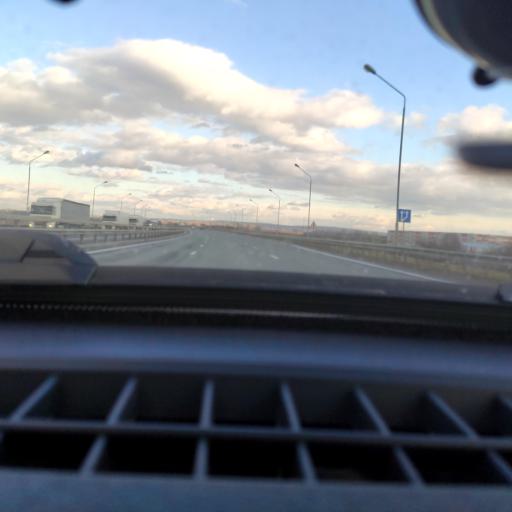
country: RU
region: Bashkortostan
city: Ufa
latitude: 54.6429
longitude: 55.9421
